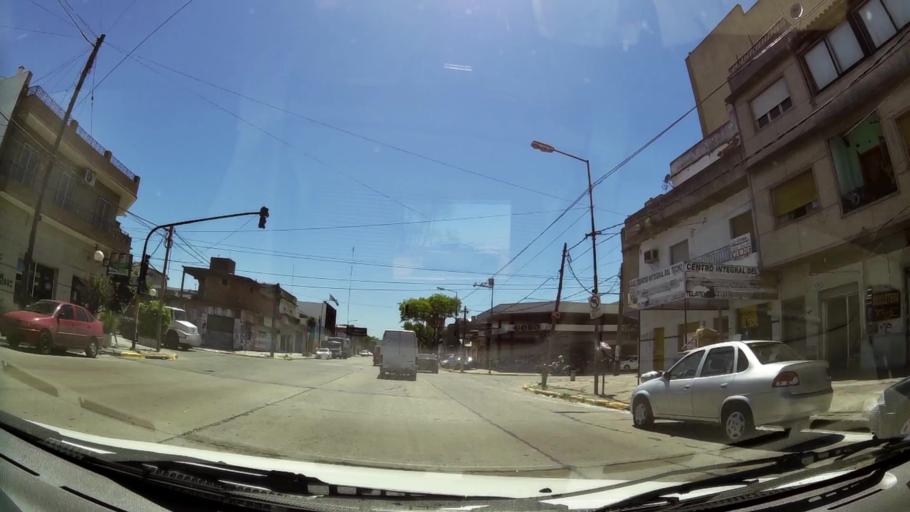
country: AR
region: Buenos Aires
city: Caseros
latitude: -34.5834
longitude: -58.5566
